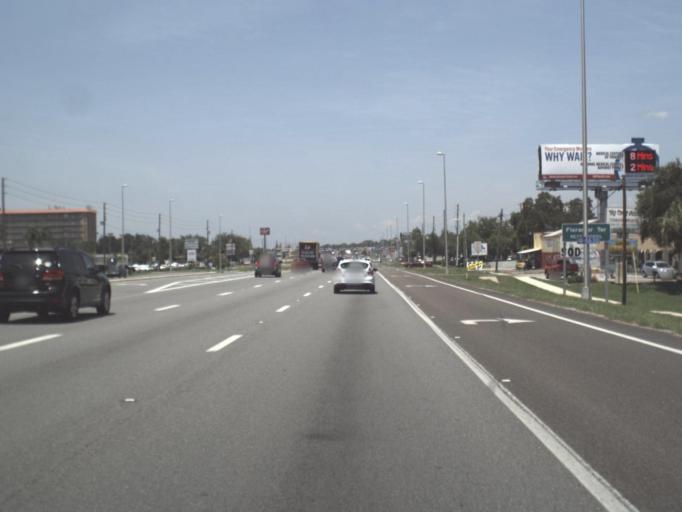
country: US
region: Florida
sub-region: Pasco County
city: Elfers
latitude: 28.2259
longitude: -82.7328
